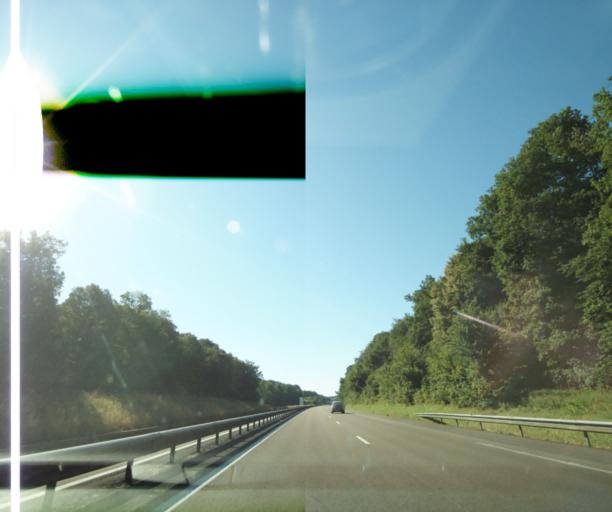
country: FR
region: Champagne-Ardenne
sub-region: Departement de l'Aube
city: Lusigny-sur-Barse
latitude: 48.1940
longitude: 4.2708
